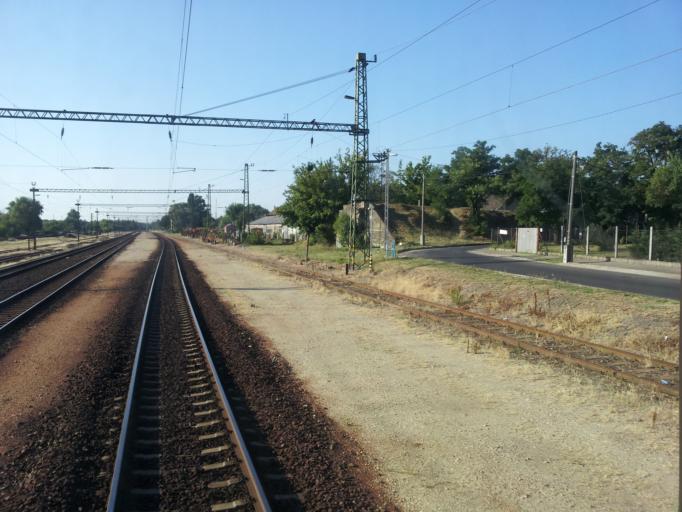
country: HU
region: Budapest
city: Budapest XXIII. keruelet
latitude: 47.4058
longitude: 19.1209
